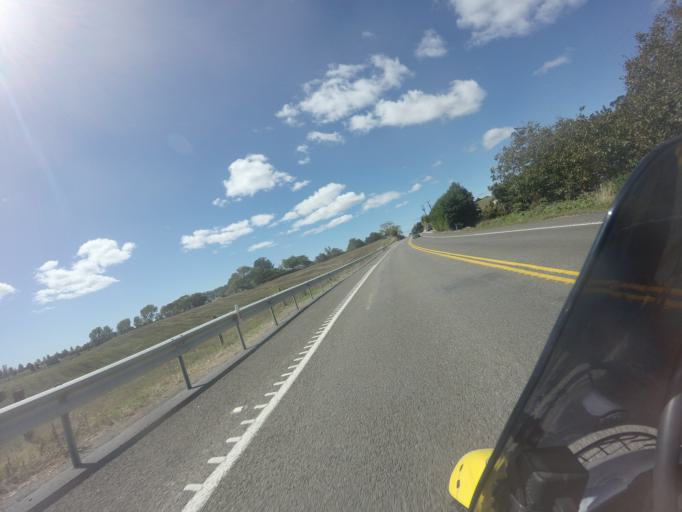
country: NZ
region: Bay of Plenty
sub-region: Whakatane District
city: Edgecumbe
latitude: -37.9985
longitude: 176.8731
